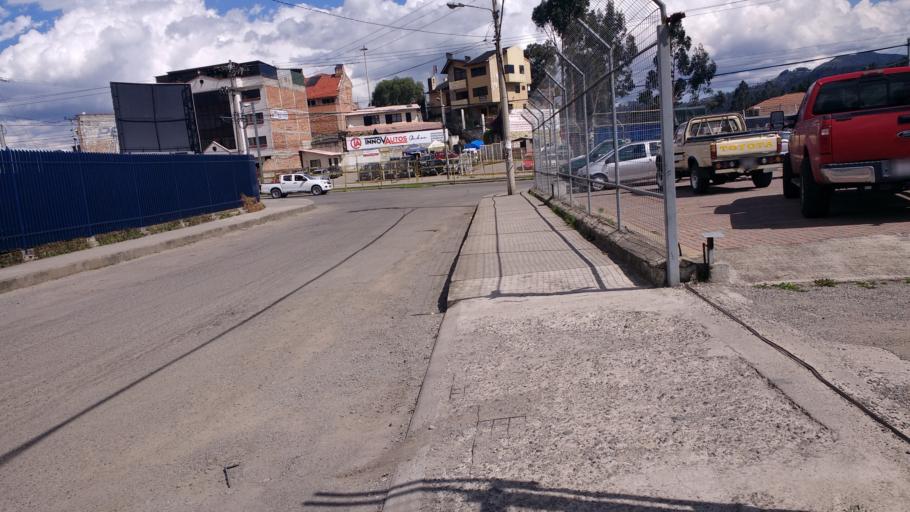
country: EC
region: Azuay
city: Cuenca
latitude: -2.9033
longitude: -79.0318
